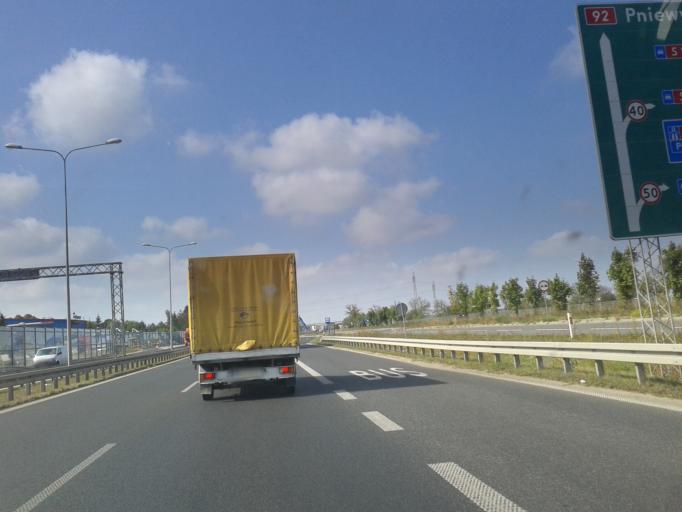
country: PL
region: Greater Poland Voivodeship
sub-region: Powiat poznanski
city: Baranowo
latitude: 52.4413
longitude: 16.7493
